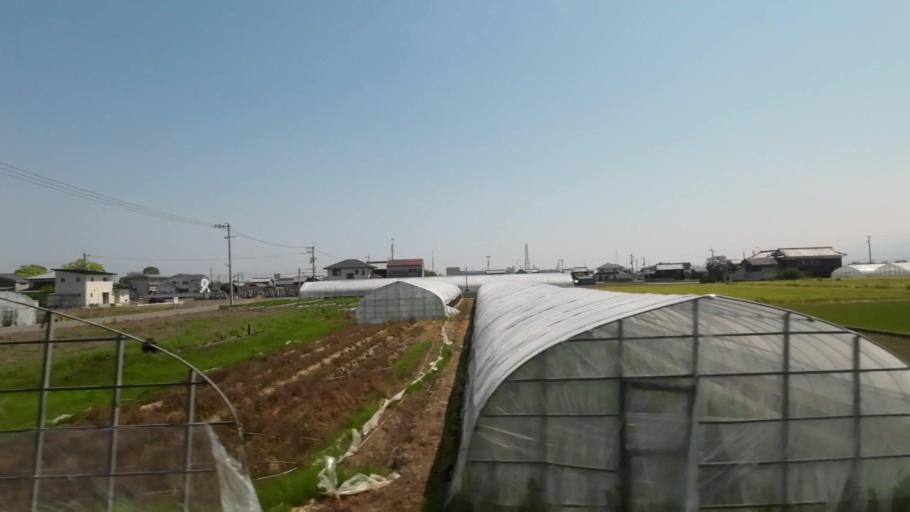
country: JP
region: Ehime
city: Saijo
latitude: 33.9237
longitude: 133.0909
